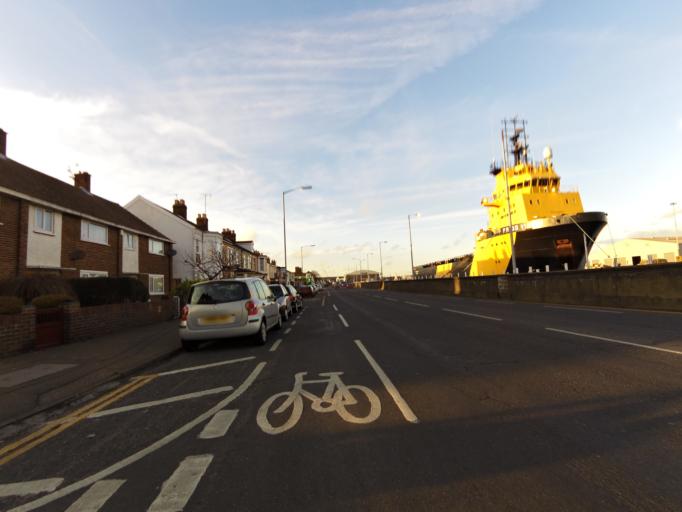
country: GB
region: England
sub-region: Norfolk
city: Great Yarmouth
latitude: 52.5932
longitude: 1.7251
